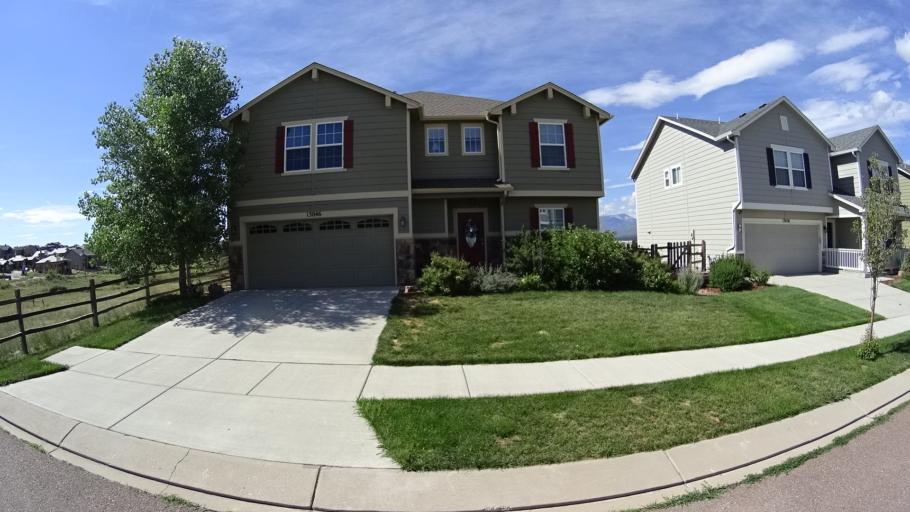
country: US
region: Colorado
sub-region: El Paso County
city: Gleneagle
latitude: 39.0227
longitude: -104.8095
